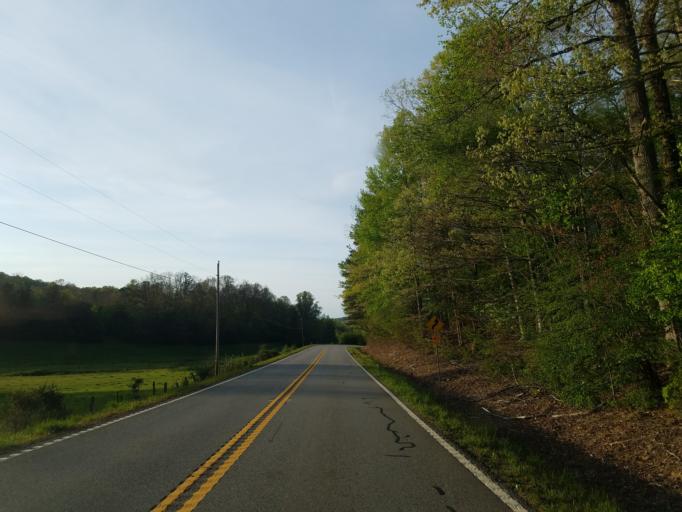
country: US
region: Georgia
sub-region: Fannin County
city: Blue Ridge
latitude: 34.8281
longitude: -84.1903
